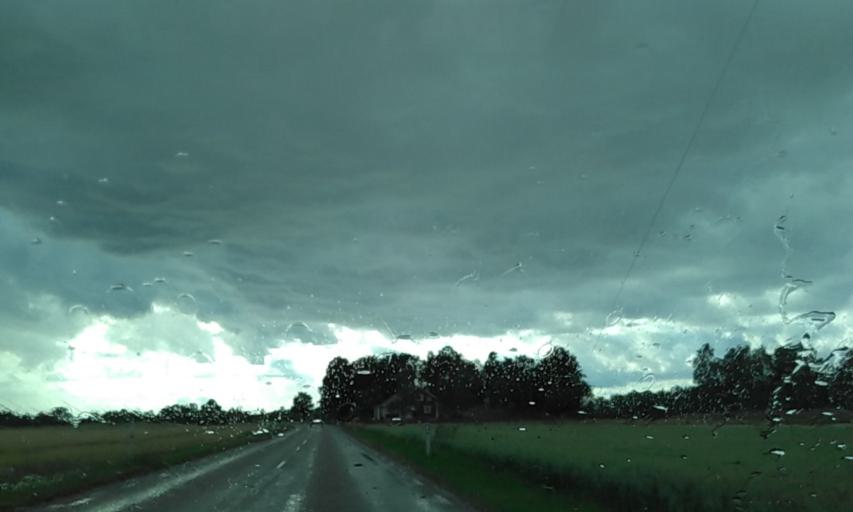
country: SE
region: Vaestra Goetaland
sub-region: Vara Kommun
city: Vara
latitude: 58.4805
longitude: 12.8803
